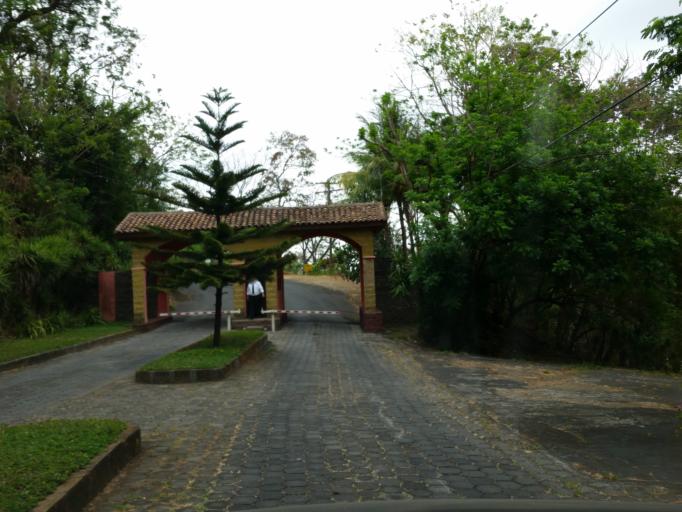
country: NI
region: Masaya
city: Ticuantepe
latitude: 12.0539
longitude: -86.2686
